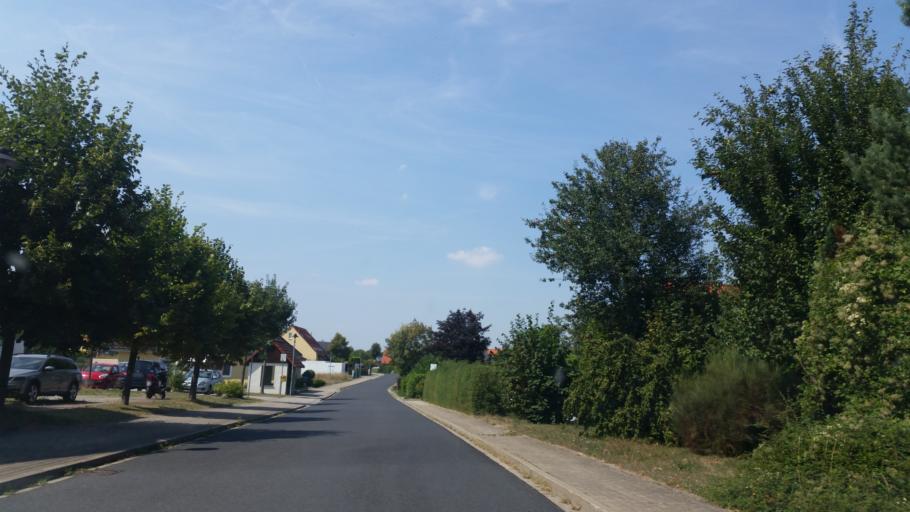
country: DE
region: Saxony
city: Klipphausen
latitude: 51.0731
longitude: 13.5265
